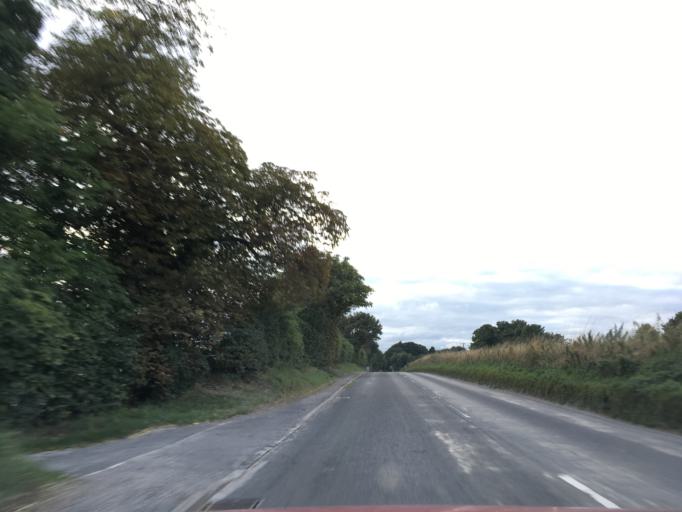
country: GB
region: England
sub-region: Wiltshire
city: Devizes
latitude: 51.3386
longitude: -1.9636
